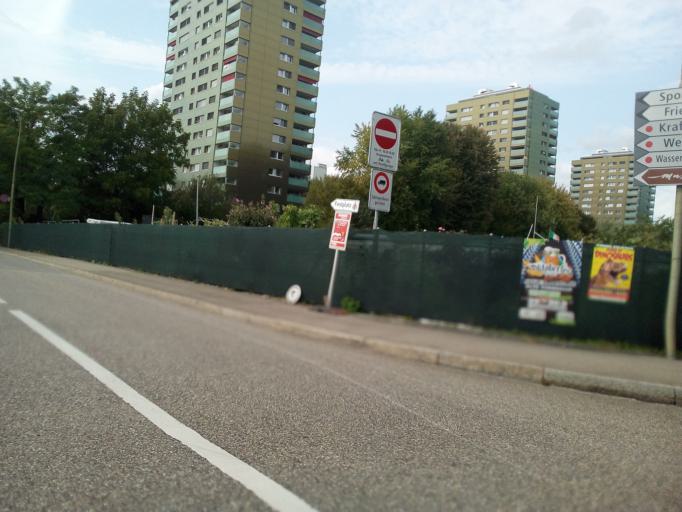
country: CH
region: Basel-Landschaft
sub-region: Bezirk Arlesheim
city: Birsfelden
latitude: 47.5551
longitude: 7.6332
